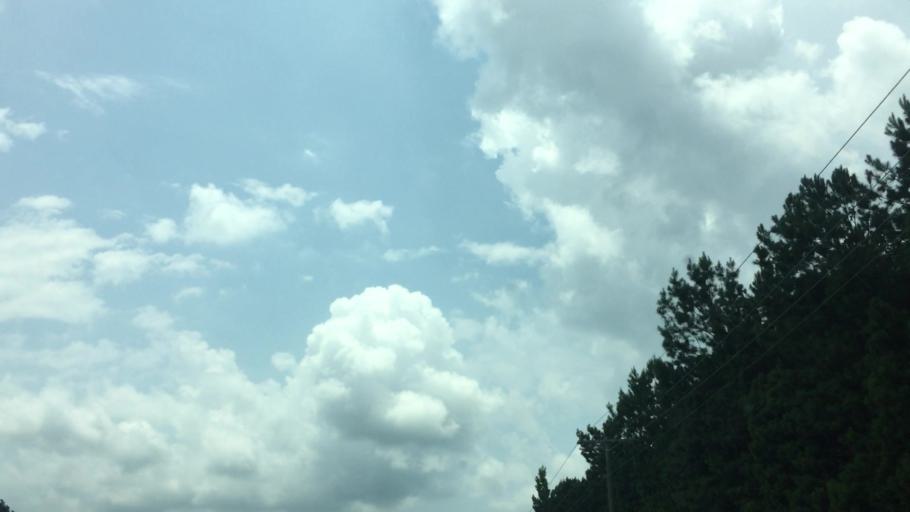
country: US
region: Georgia
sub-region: Fulton County
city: Fairburn
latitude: 33.5928
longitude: -84.6435
